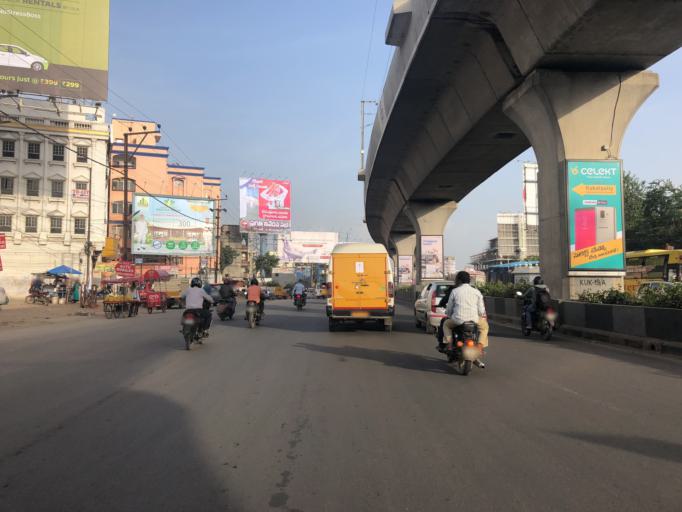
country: IN
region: Telangana
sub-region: Rangareddi
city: Kukatpalli
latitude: 17.4820
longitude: 78.4156
